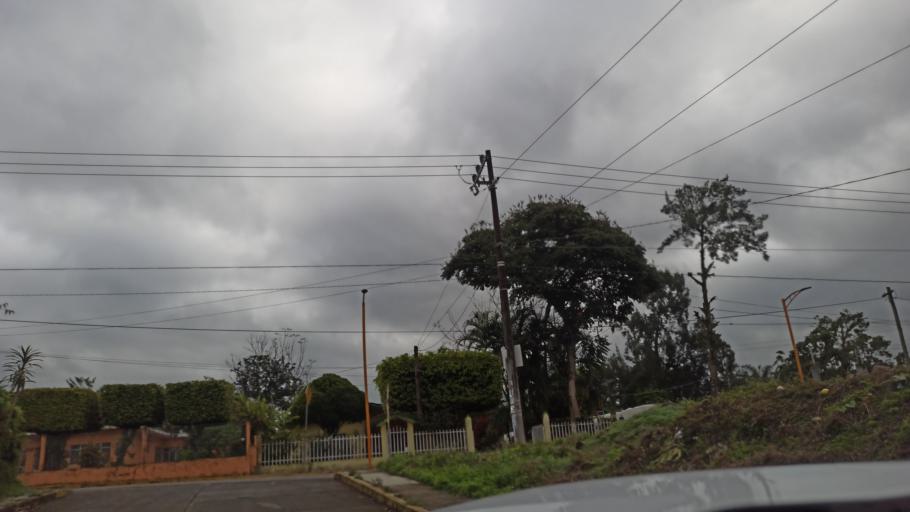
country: MX
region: Veracruz
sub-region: Chocaman
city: San Jose Neria
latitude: 19.0016
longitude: -97.0040
